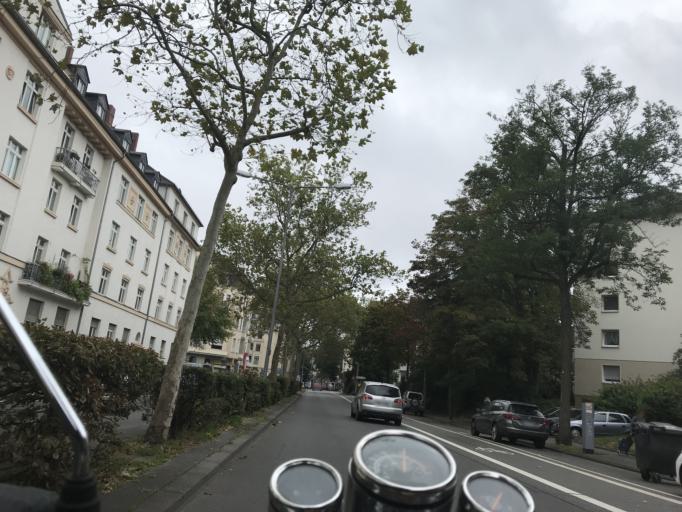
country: DE
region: Hesse
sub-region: Regierungsbezirk Darmstadt
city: Wiesbaden
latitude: 50.0786
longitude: 8.2249
